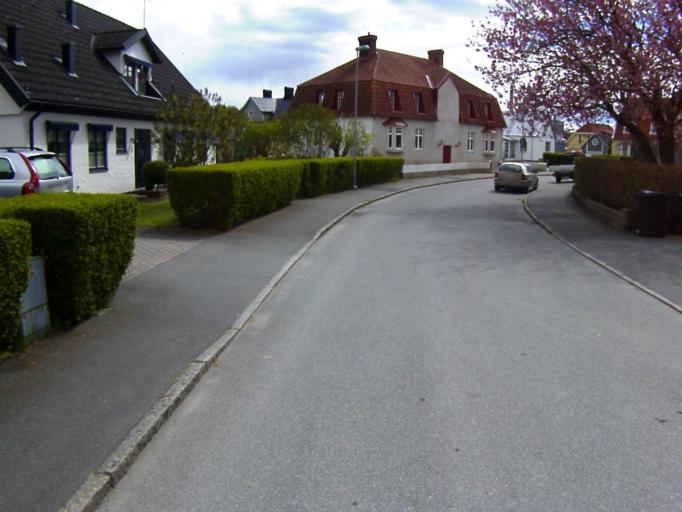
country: SE
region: Skane
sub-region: Kristianstads Kommun
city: Kristianstad
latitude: 56.0386
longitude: 14.1716
